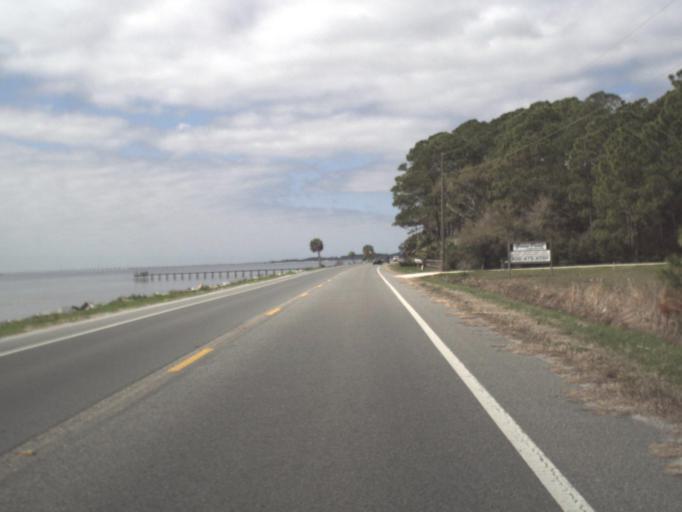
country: US
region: Florida
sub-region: Franklin County
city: Eastpoint
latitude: 29.7527
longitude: -84.8440
